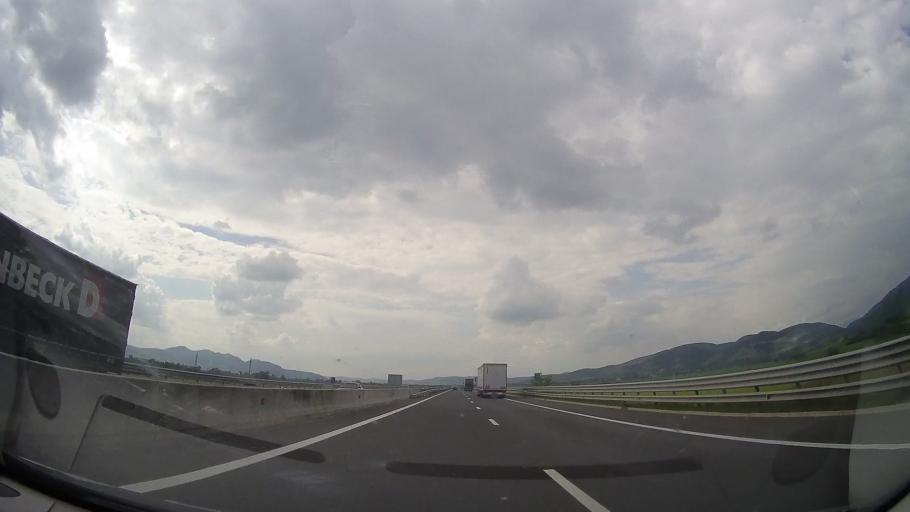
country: RO
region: Hunedoara
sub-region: Oras Simeria
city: Simeria
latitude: 45.8713
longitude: 23.0148
